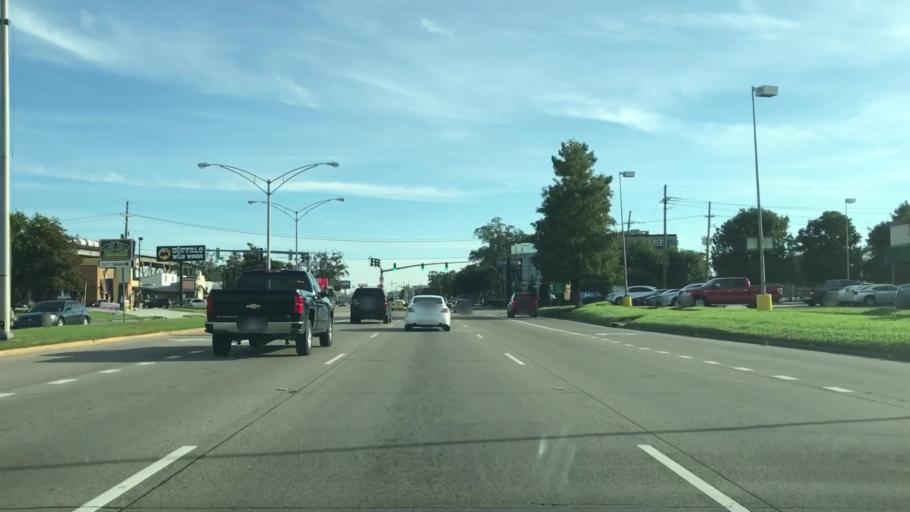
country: US
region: Louisiana
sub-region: Jefferson Parish
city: Elmwood
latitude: 29.9592
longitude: -90.1836
